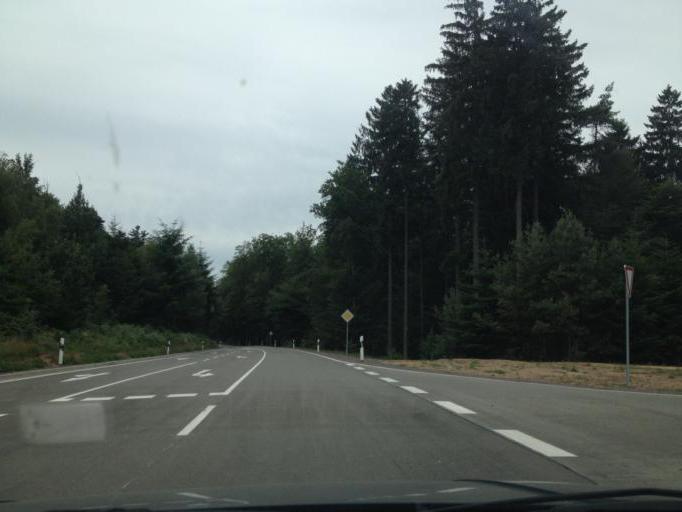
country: DE
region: Rheinland-Pfalz
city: Waldleiningen
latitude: 49.3146
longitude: 7.8555
